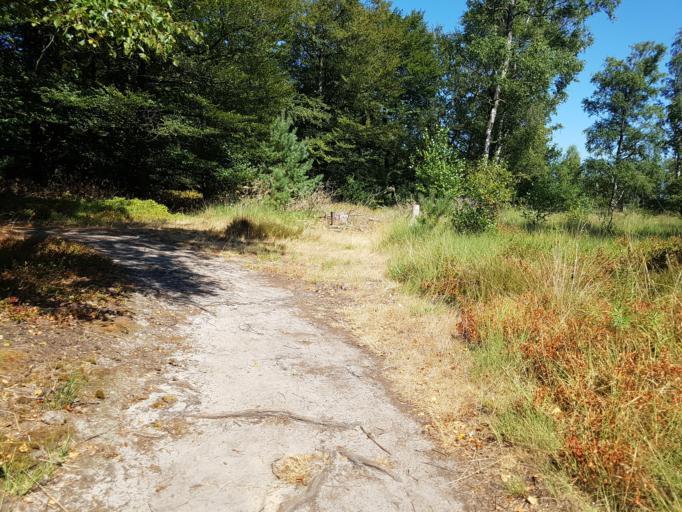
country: NL
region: North Brabant
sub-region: Gemeente Haaren
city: Haaren
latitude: 51.5835
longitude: 5.2582
